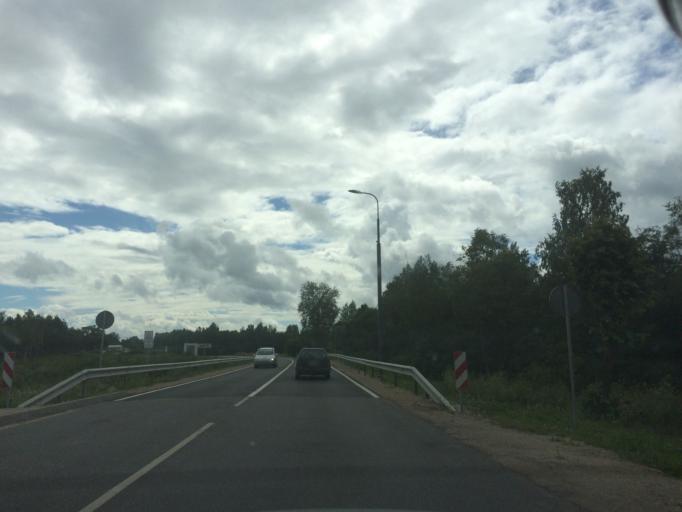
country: LV
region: Rezekne
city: Rezekne
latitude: 56.4918
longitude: 27.3162
